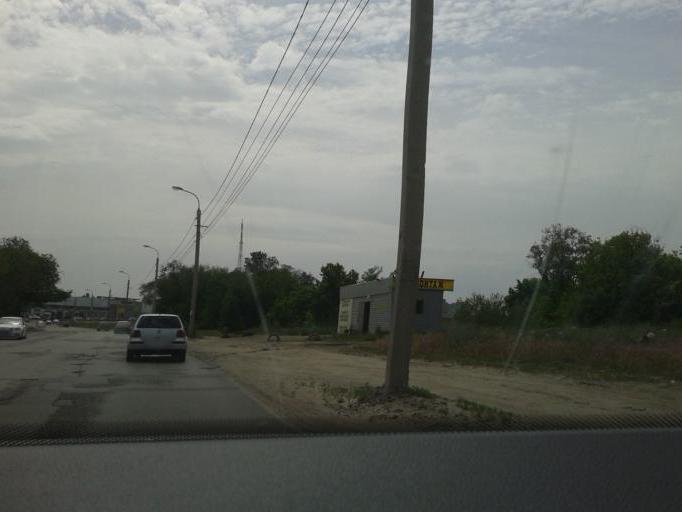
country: RU
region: Volgograd
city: Volgograd
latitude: 48.7533
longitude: 44.5247
